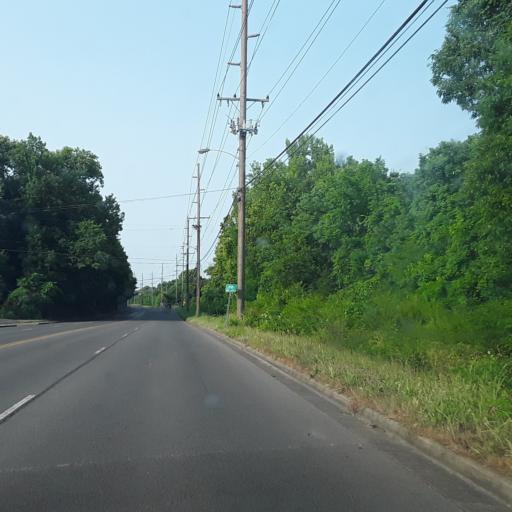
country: US
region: Tennessee
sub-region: Williamson County
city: Brentwood
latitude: 36.0580
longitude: -86.7418
